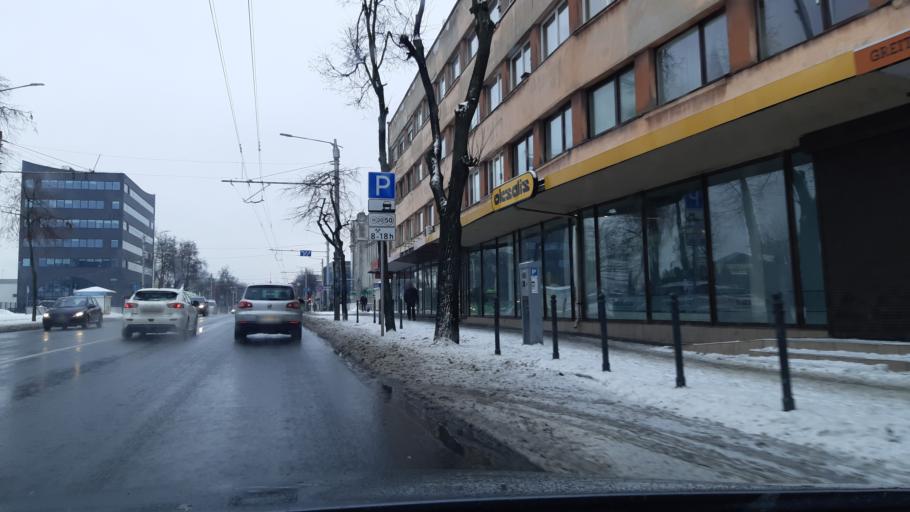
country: LT
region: Kauno apskritis
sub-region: Kaunas
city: Kaunas
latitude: 54.9031
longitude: 23.9135
